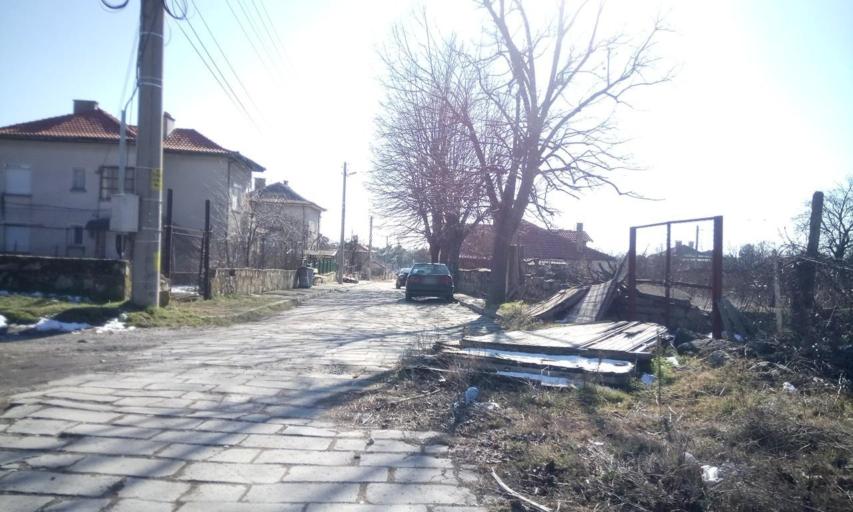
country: BG
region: Plovdiv
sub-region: Obshtina Khisarya
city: Khisarya
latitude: 42.5194
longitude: 24.7212
